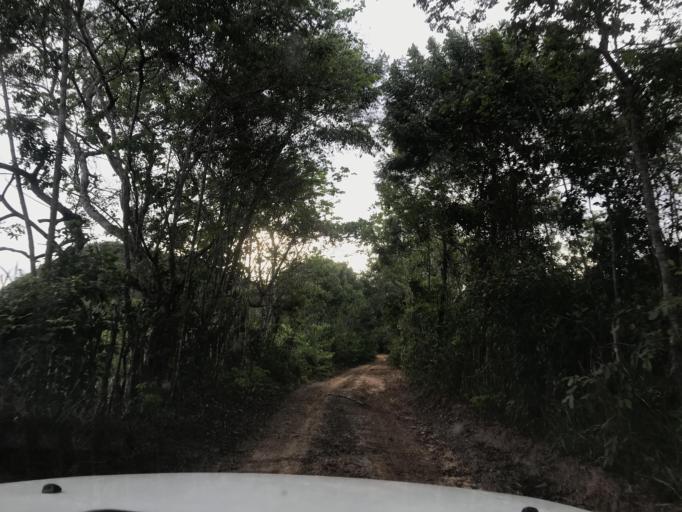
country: BR
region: Bahia
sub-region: Entre Rios
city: Entre Rios
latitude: -12.0520
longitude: -38.2170
